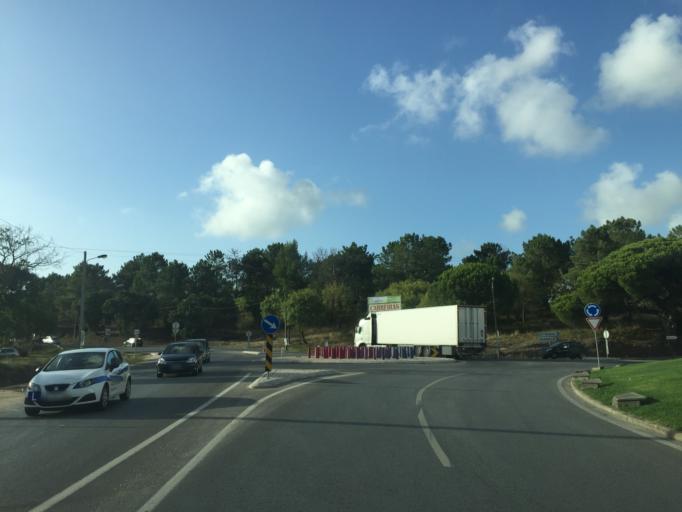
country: PT
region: Lisbon
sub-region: Torres Vedras
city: Torres Vedras
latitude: 39.1057
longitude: -9.2591
